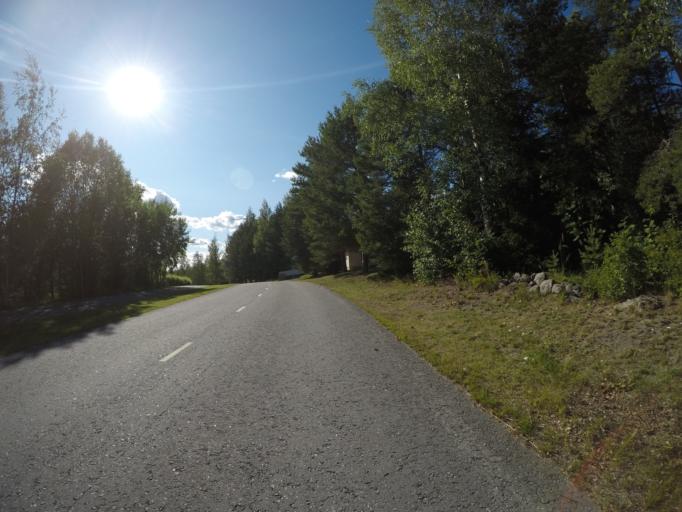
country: FI
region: Haeme
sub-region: Haemeenlinna
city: Haemeenlinna
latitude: 61.0222
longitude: 24.5177
